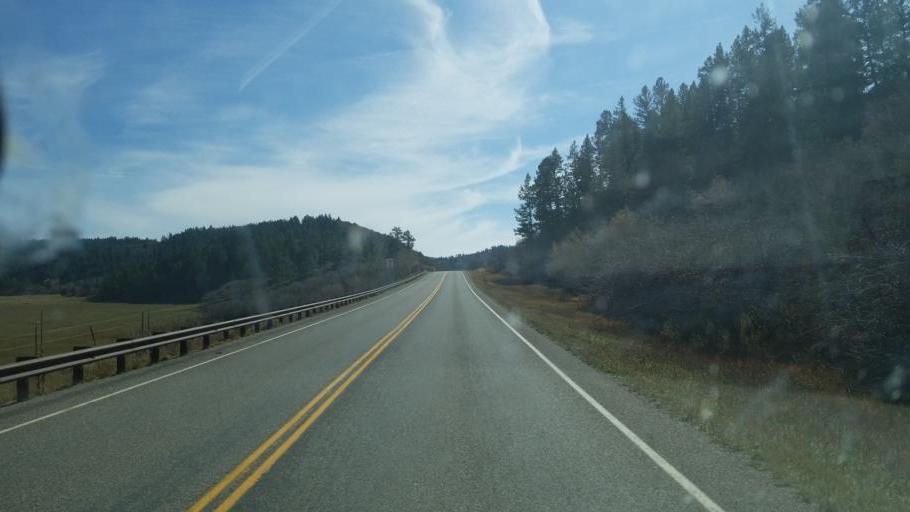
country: US
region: New Mexico
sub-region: Rio Arriba County
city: Dulce
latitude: 36.9953
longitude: -106.7847
